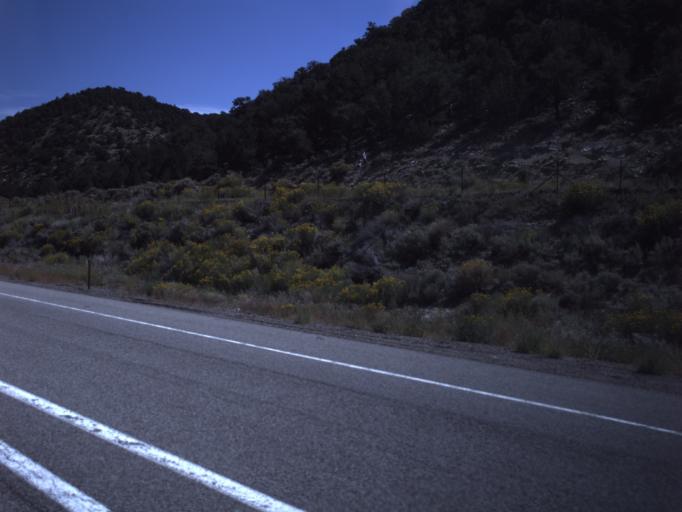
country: US
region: Utah
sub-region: Wayne County
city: Loa
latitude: 38.7573
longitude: -111.4161
